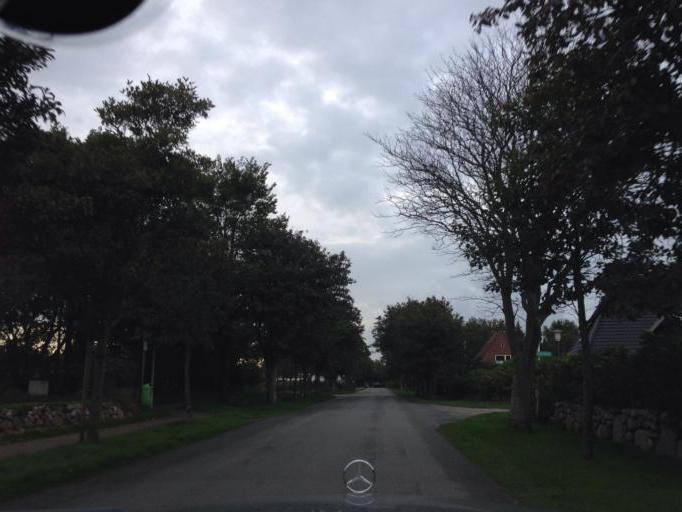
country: DE
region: Schleswig-Holstein
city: Nieblum
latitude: 54.6884
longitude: 8.4921
